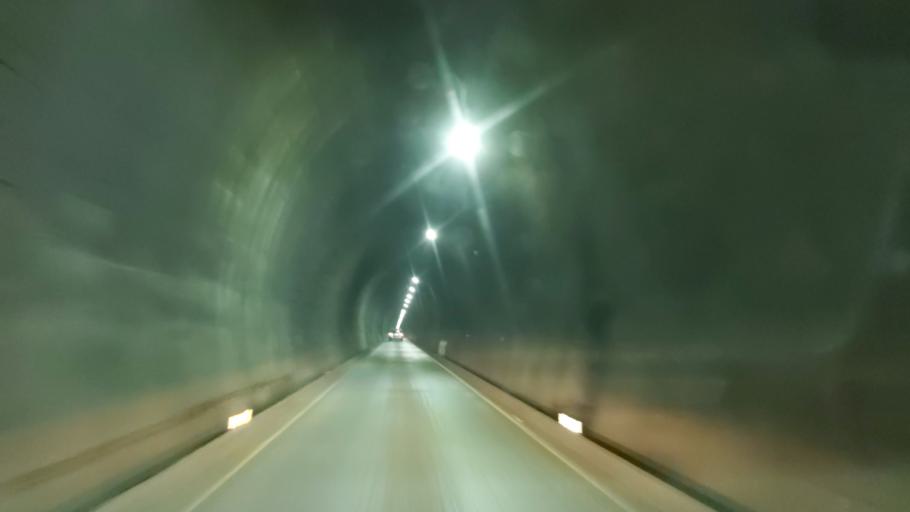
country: CL
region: Araucania
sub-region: Provincia de Cautin
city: Vilcun
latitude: -38.5345
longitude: -71.5089
